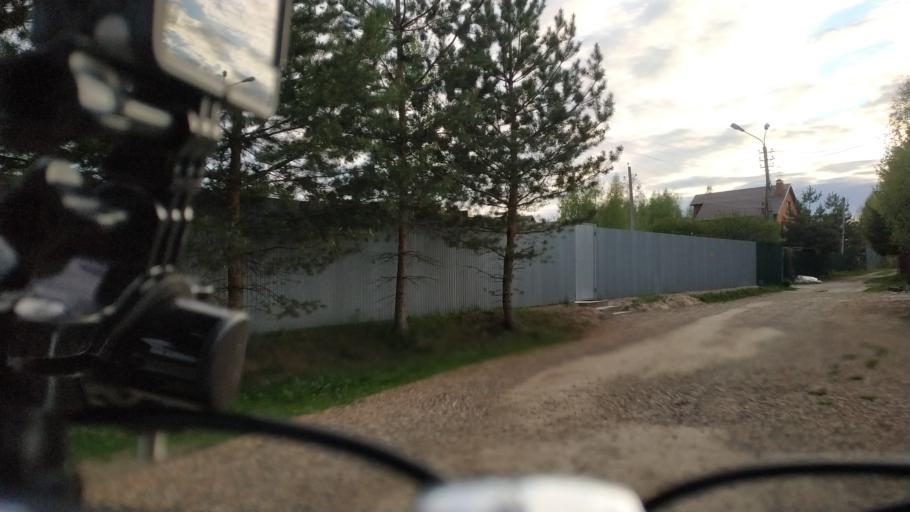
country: RU
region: Moskovskaya
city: Ramenskoye
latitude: 55.5781
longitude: 38.2647
